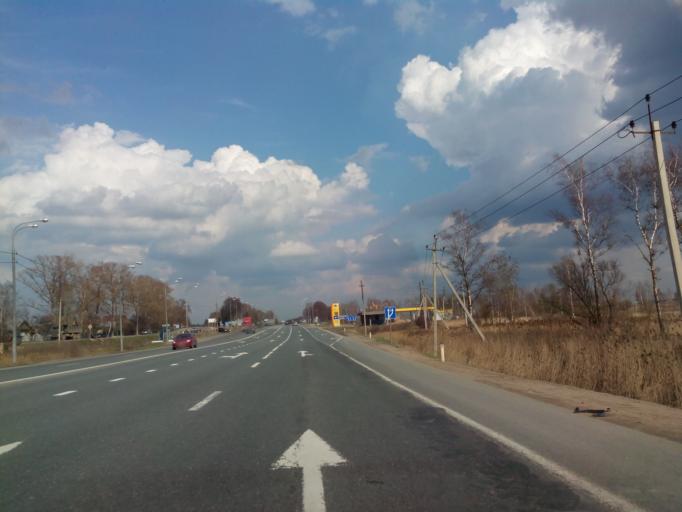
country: RU
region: Moskovskaya
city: Chupryakovo
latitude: 55.5577
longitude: 36.5679
